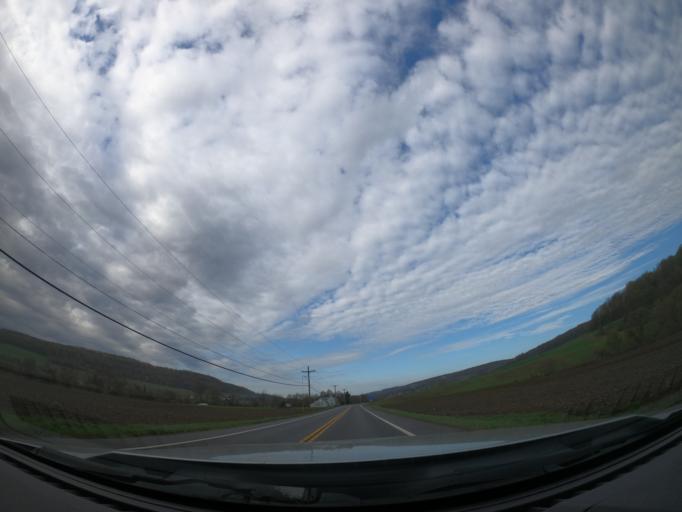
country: US
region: New York
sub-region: Cortland County
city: McGraw
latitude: 42.6743
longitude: -76.0807
